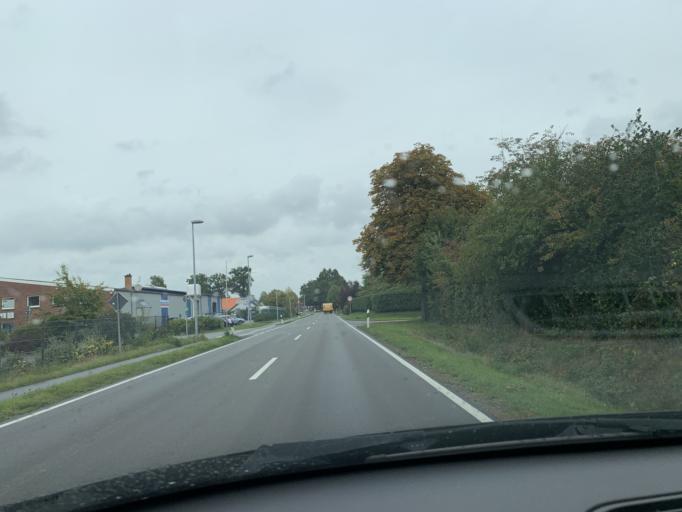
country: DE
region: Lower Saxony
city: Bad Zwischenahn
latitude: 53.1739
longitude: 8.0686
